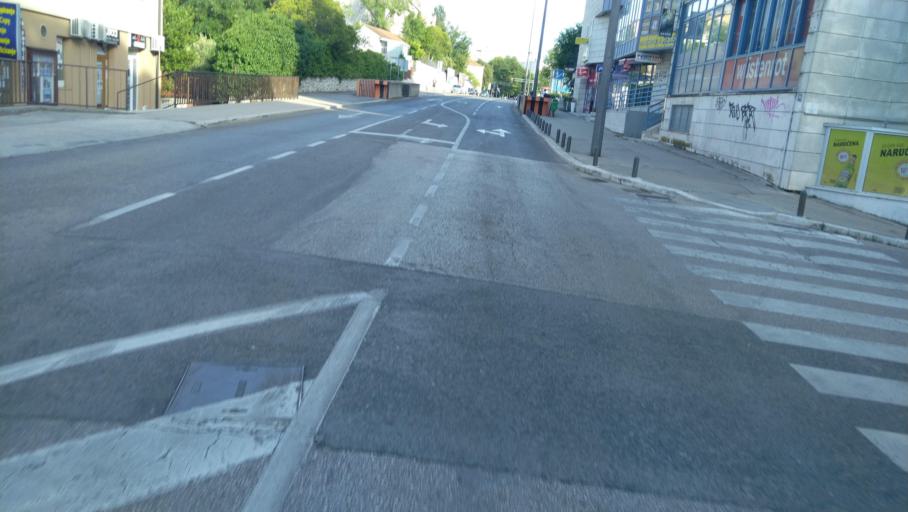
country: HR
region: Sibensko-Kniniska
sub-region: Grad Sibenik
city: Sibenik
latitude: 43.7308
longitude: 15.9005
